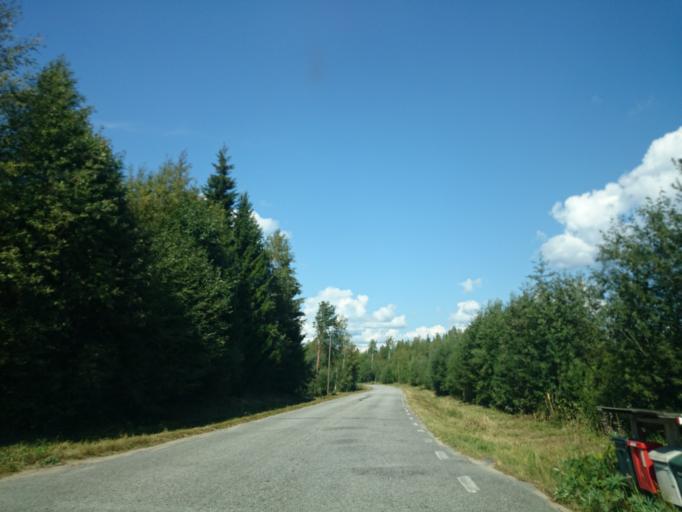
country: SE
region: Gaevleborg
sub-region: Ljusdals Kommun
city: Jaervsoe
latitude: 61.7276
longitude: 16.2021
